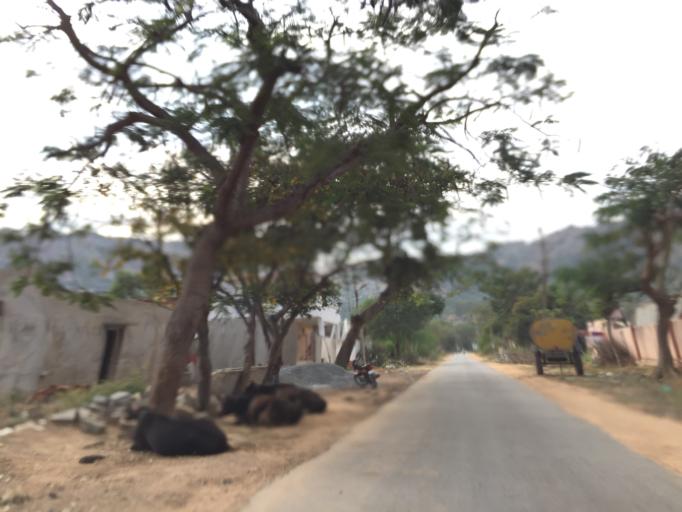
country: IN
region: Karnataka
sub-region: Kolar
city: Kolar
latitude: 13.1387
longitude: 78.1078
